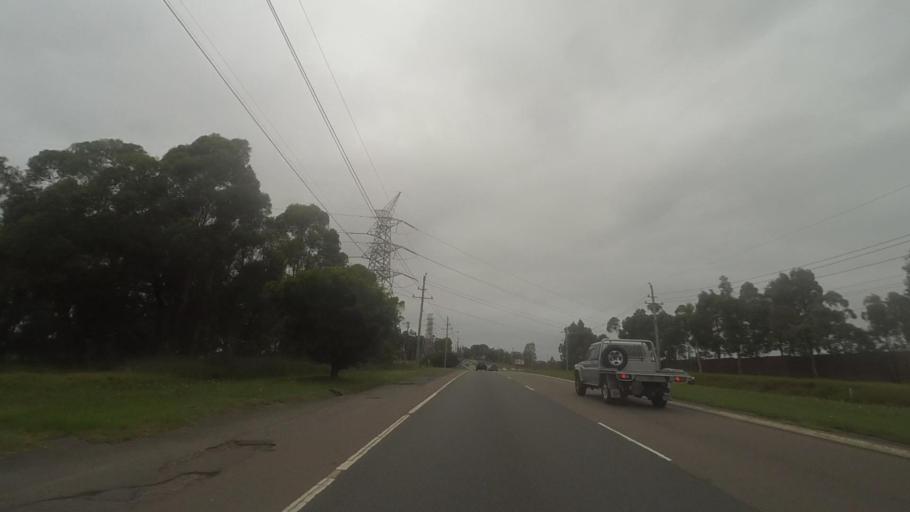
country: AU
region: New South Wales
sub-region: Newcastle
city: Mayfield West
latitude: -32.8744
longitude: 151.7125
